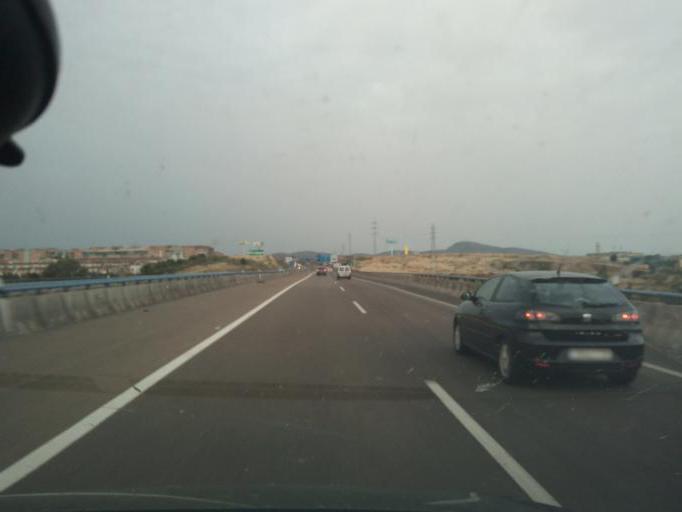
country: ES
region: Extremadura
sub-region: Provincia de Badajoz
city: Merida
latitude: 38.9290
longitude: -6.3685
